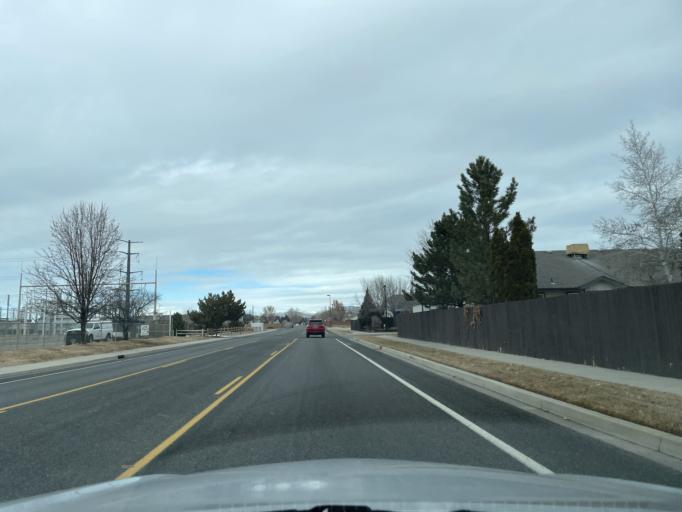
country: US
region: Colorado
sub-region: Mesa County
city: Grand Junction
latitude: 39.0976
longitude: -108.5801
